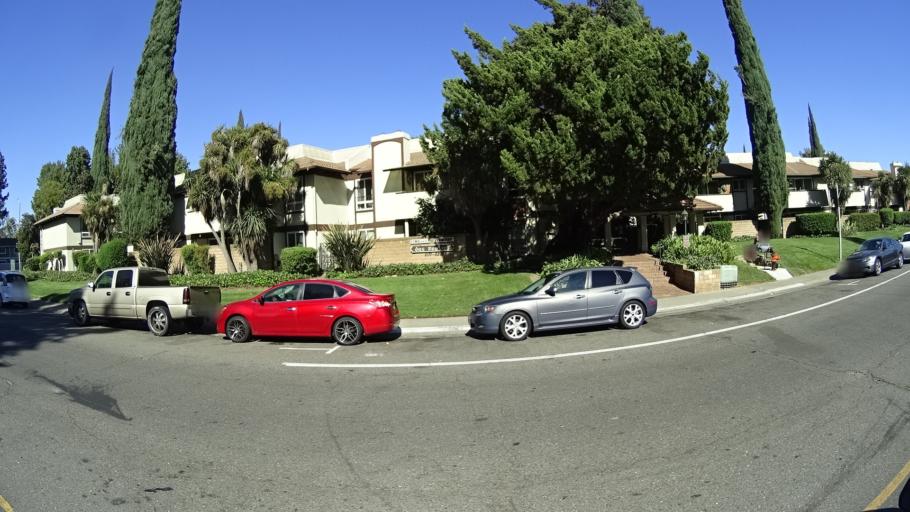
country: US
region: California
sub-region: Yolo County
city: West Sacramento
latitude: 38.5141
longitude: -121.5269
